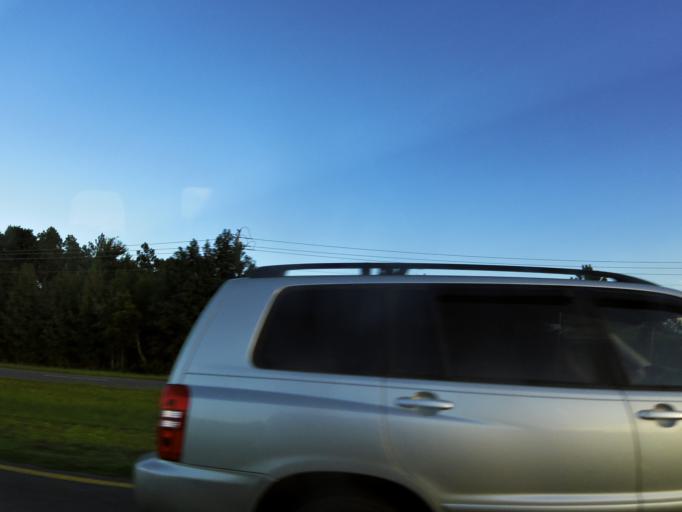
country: US
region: Georgia
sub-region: Camden County
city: St Marys
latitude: 30.7800
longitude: -81.6224
